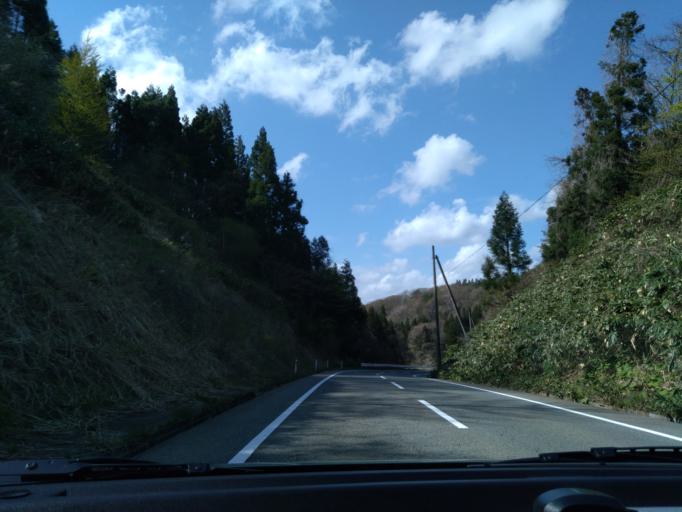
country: JP
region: Akita
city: Akita
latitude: 39.6962
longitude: 140.2213
